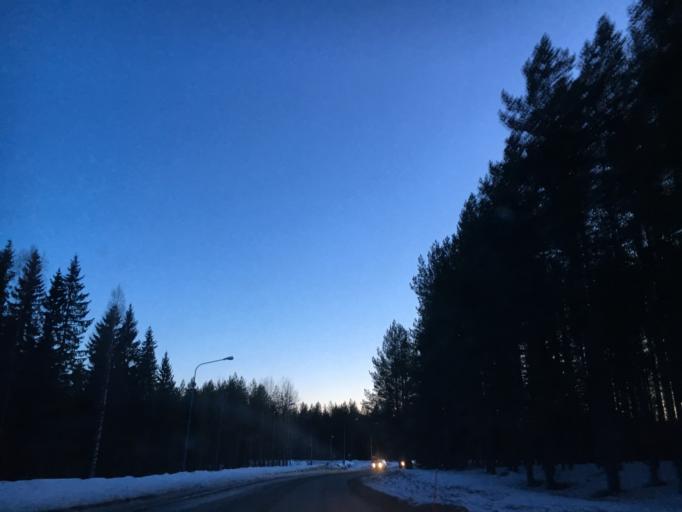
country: FI
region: Kainuu
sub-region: Kajaani
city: Kajaani
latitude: 64.1964
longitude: 27.7540
